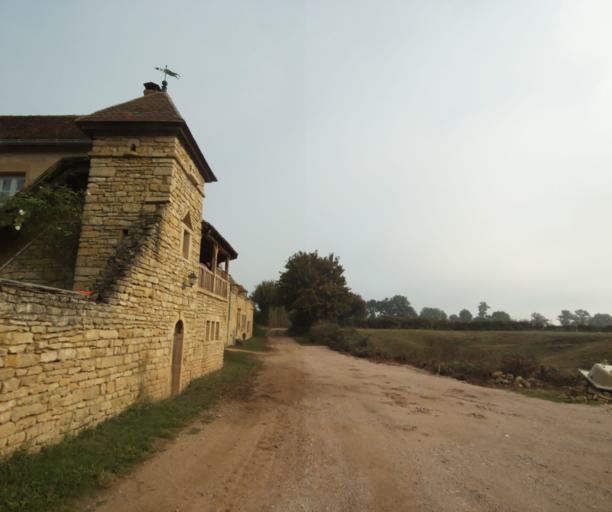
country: FR
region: Bourgogne
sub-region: Departement de Saone-et-Loire
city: Charolles
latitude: 46.4536
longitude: 4.2891
